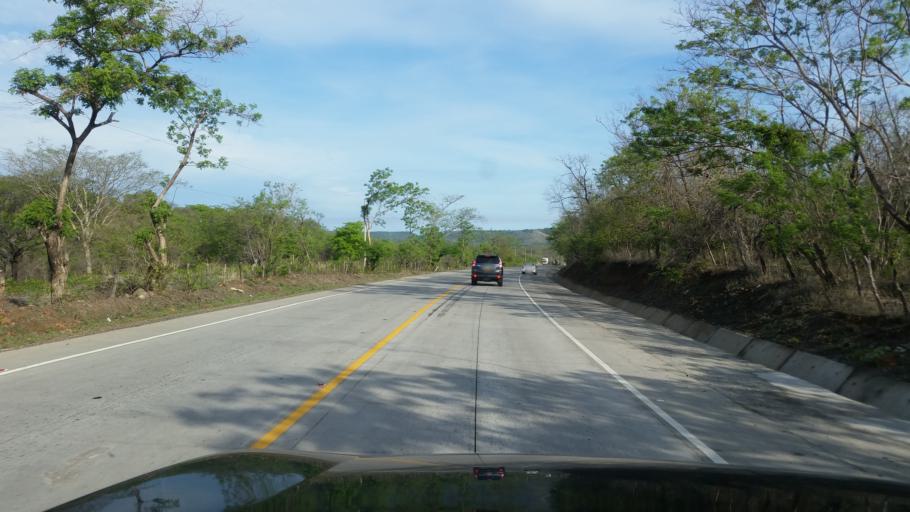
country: NI
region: Leon
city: Nagarote
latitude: 12.1206
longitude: -86.6263
